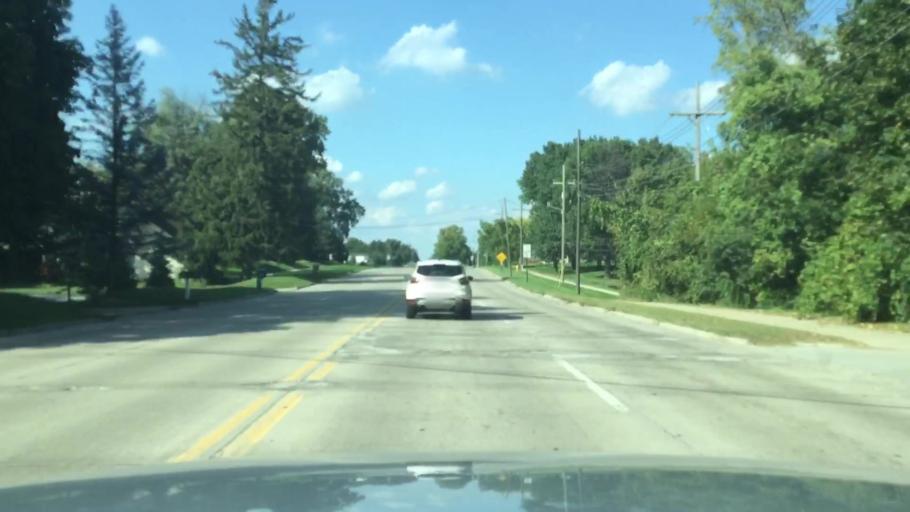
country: US
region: Michigan
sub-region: Wayne County
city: Westland
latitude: 42.3391
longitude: -83.4093
